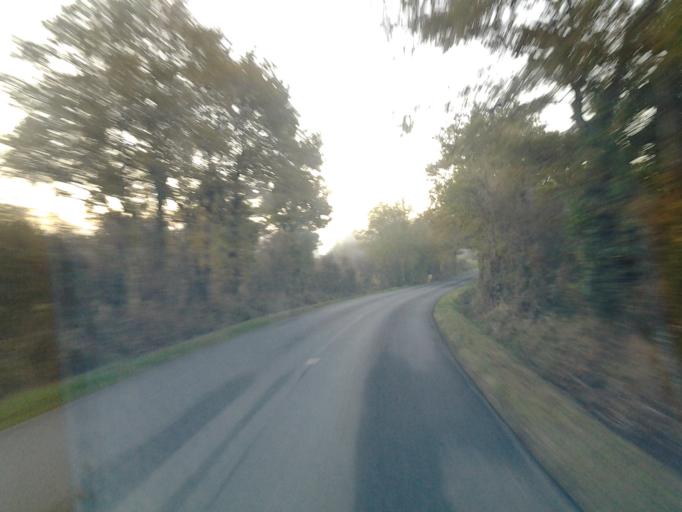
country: FR
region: Pays de la Loire
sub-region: Departement de la Vendee
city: Chateau-Guibert
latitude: 46.6323
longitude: -1.2331
